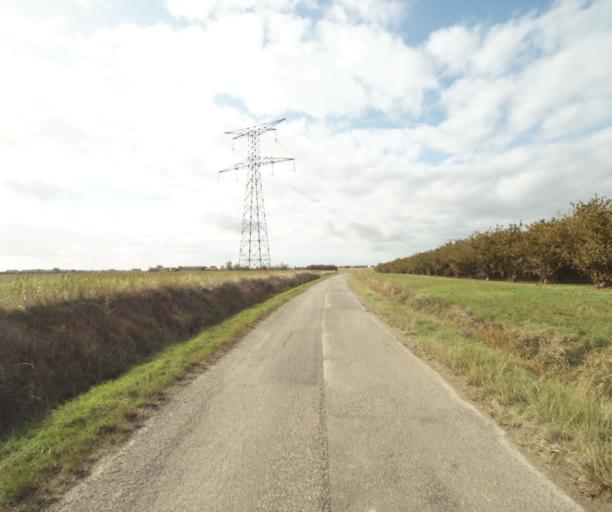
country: FR
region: Midi-Pyrenees
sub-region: Departement du Tarn-et-Garonne
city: Finhan
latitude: 43.8996
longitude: 1.1188
